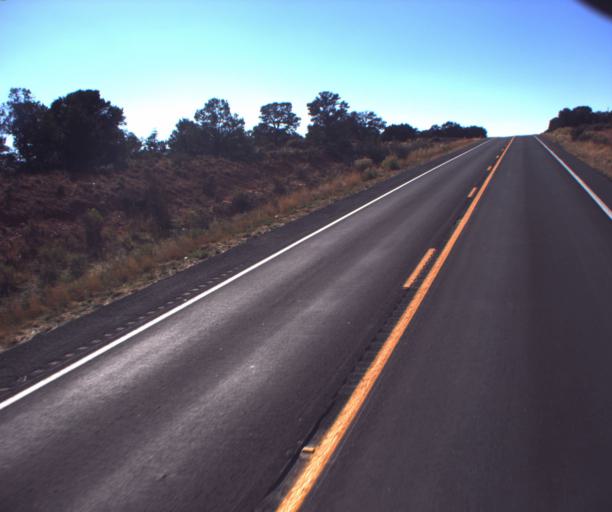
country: US
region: Arizona
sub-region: Coconino County
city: Kaibito
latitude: 36.5841
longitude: -110.8288
